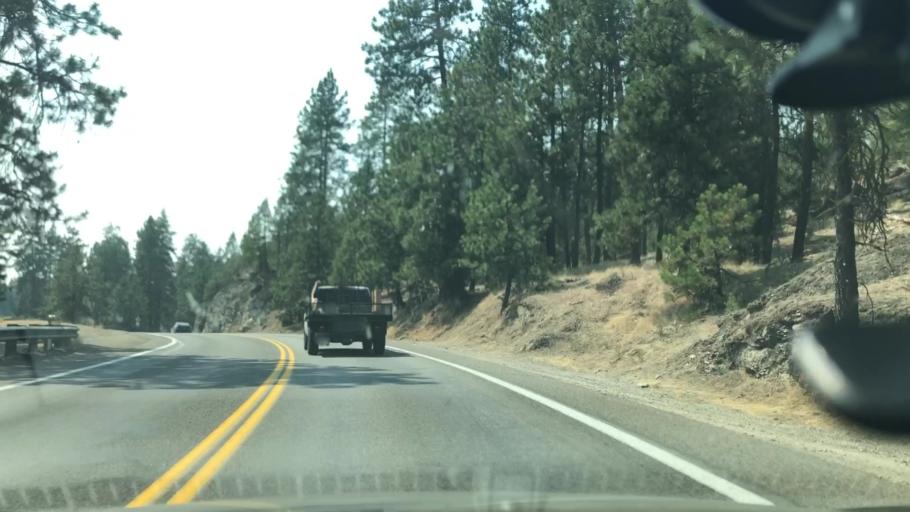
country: US
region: Washington
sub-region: Spokane County
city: Millwood
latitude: 47.6955
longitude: -117.3066
